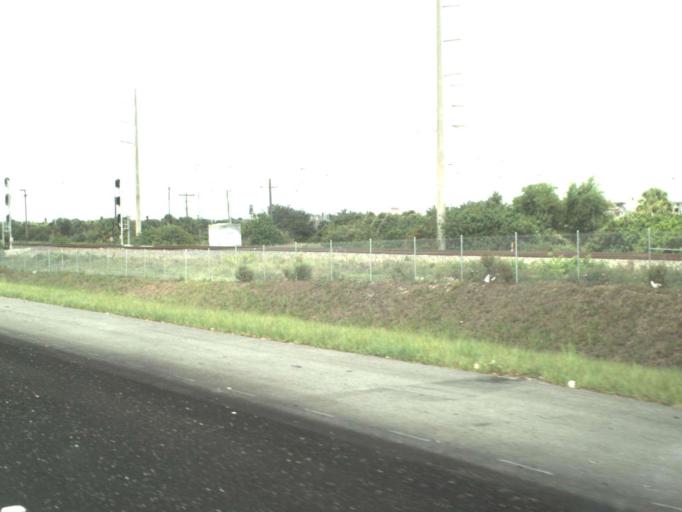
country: US
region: Florida
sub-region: Palm Beach County
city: Boca Raton
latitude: 26.3845
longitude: -80.1074
